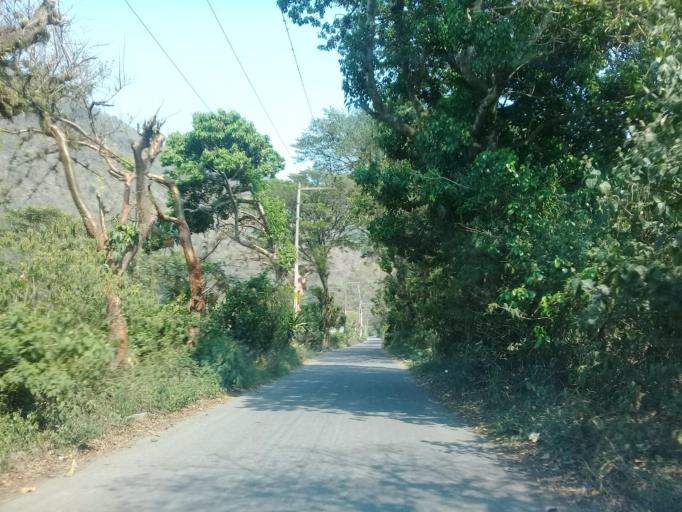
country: MX
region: Veracruz
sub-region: Ixtaczoquitlan
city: Campo Chico
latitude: 18.8339
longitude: -97.0204
